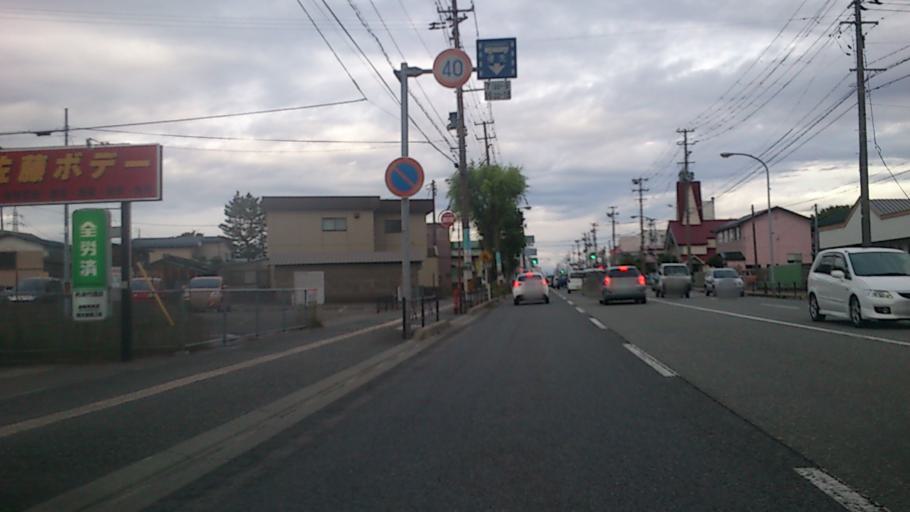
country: JP
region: Akita
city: Akita Shi
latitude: 39.7481
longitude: 140.0776
